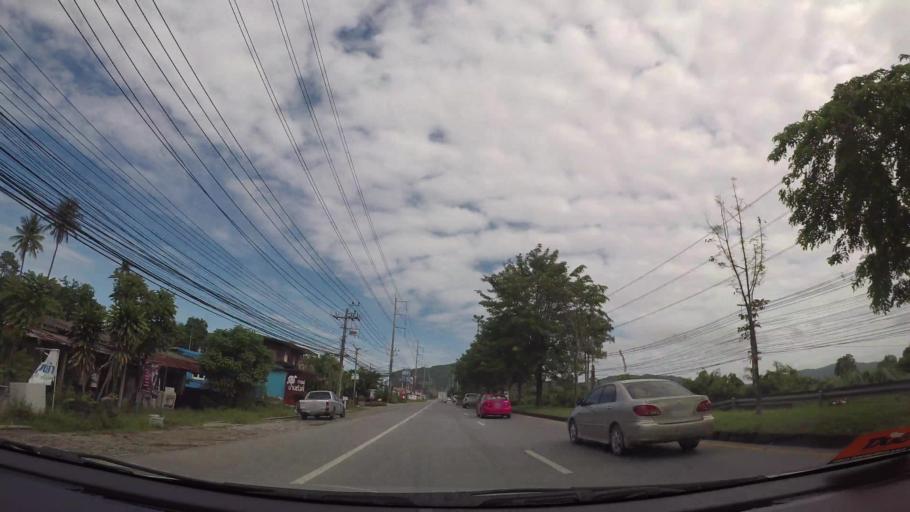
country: TH
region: Rayong
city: Ban Chang
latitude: 12.7438
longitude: 101.1160
